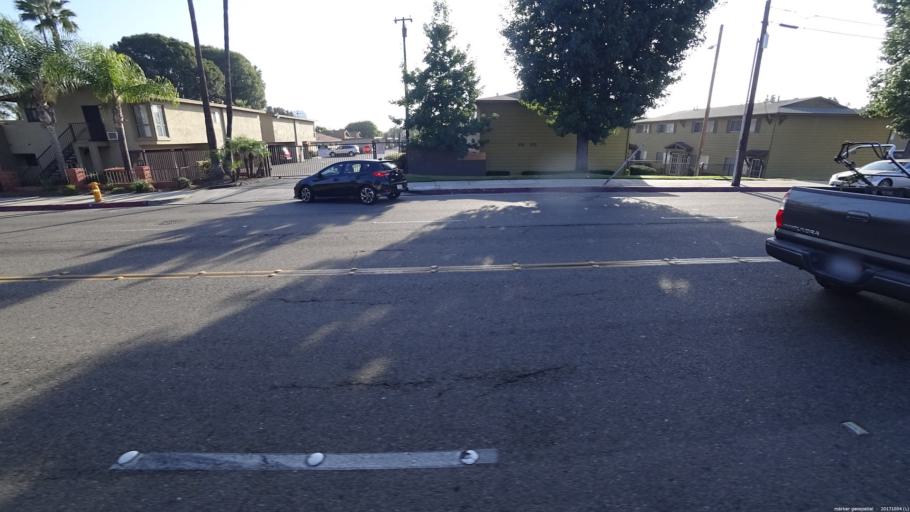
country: US
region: California
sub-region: Orange County
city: Garden Grove
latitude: 33.7835
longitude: -117.9062
